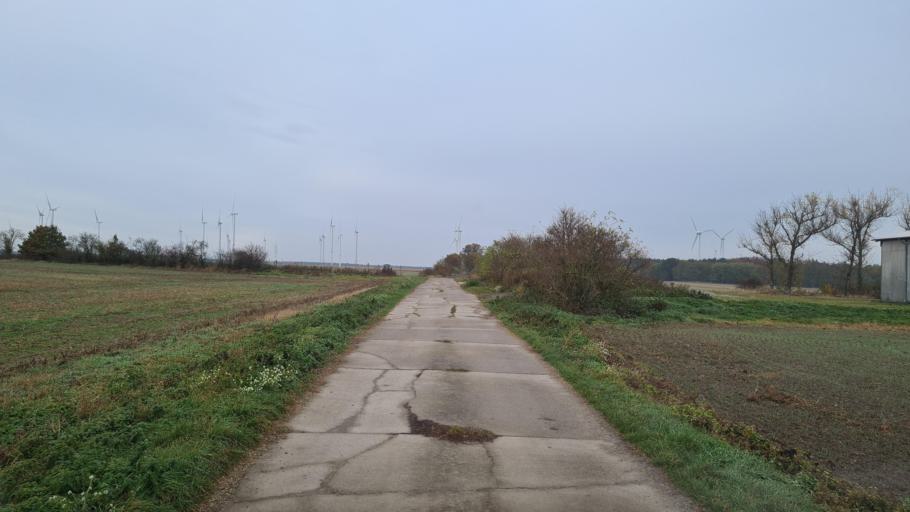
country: DE
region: Brandenburg
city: Niedergorsdorf
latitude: 51.9952
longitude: 12.8887
